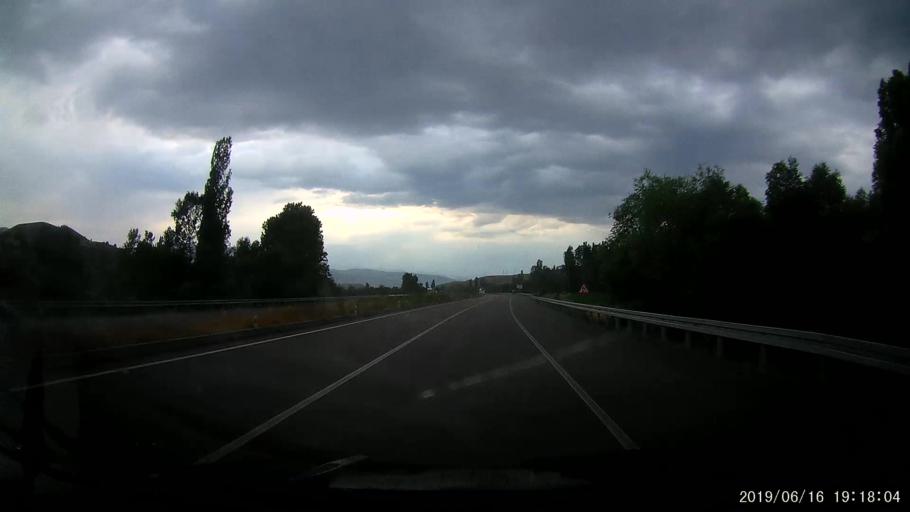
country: TR
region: Sivas
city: Akincilar
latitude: 40.0945
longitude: 38.4682
